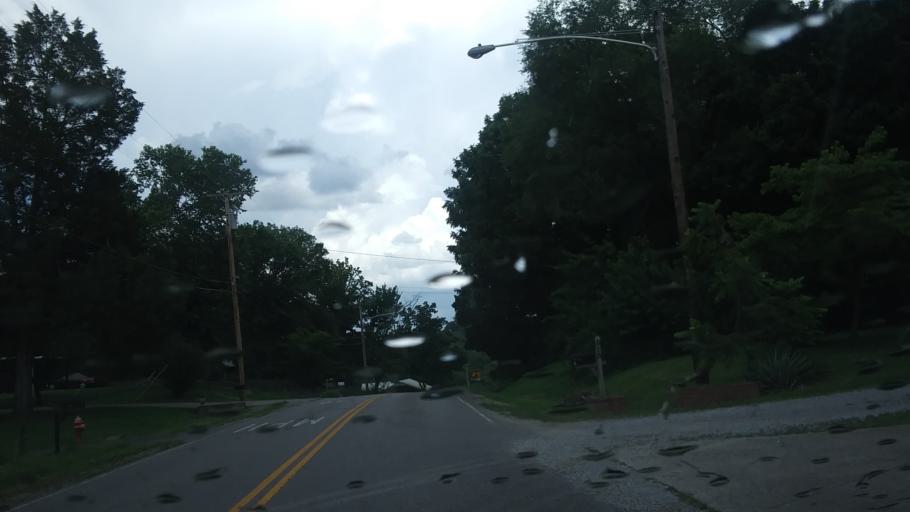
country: US
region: Tennessee
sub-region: Davidson County
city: Oak Hill
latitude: 36.0633
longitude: -86.7060
